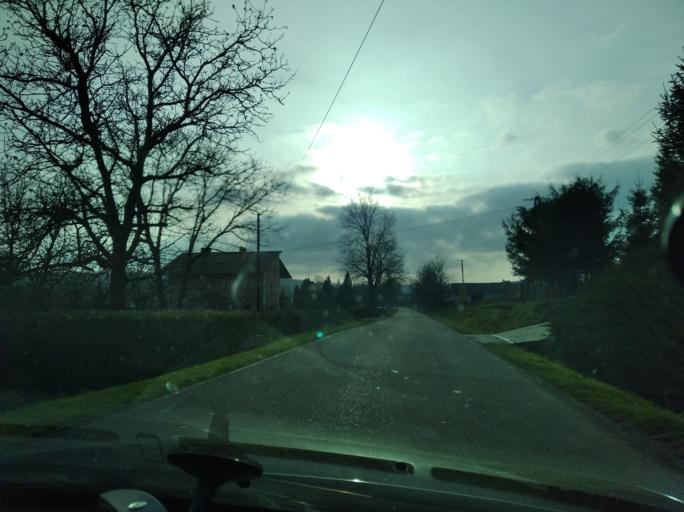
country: PL
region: Subcarpathian Voivodeship
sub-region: Powiat przeworski
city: Lopuszka Wielka
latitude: 49.9464
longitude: 22.4066
